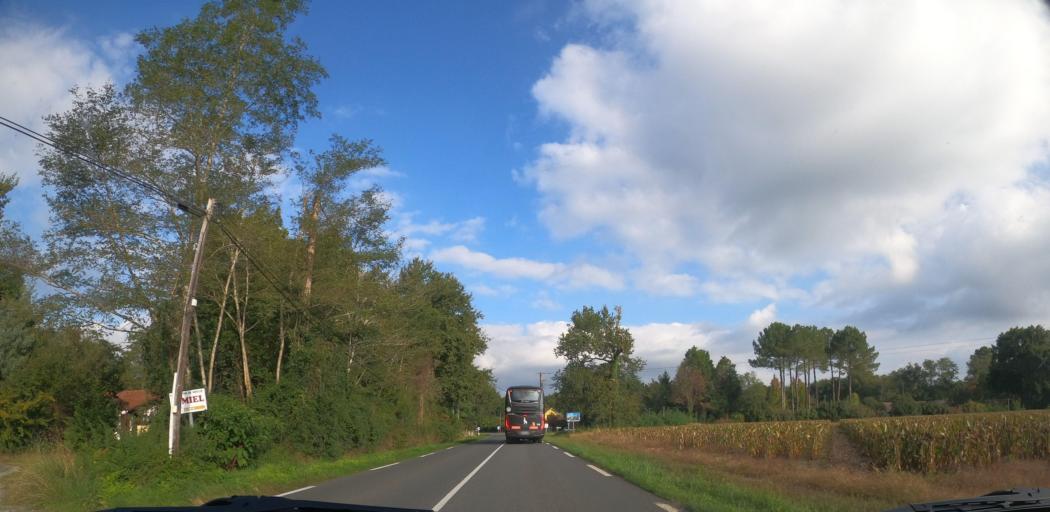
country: FR
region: Aquitaine
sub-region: Departement des Landes
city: Soustons
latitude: 43.7322
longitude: -1.2878
